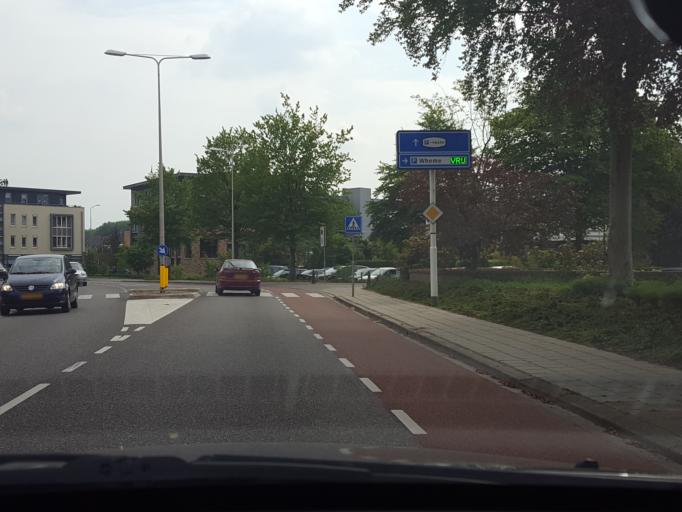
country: NL
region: Gelderland
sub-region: Gemeente Winterswijk
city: Winterswijk
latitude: 51.9701
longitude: 6.7231
